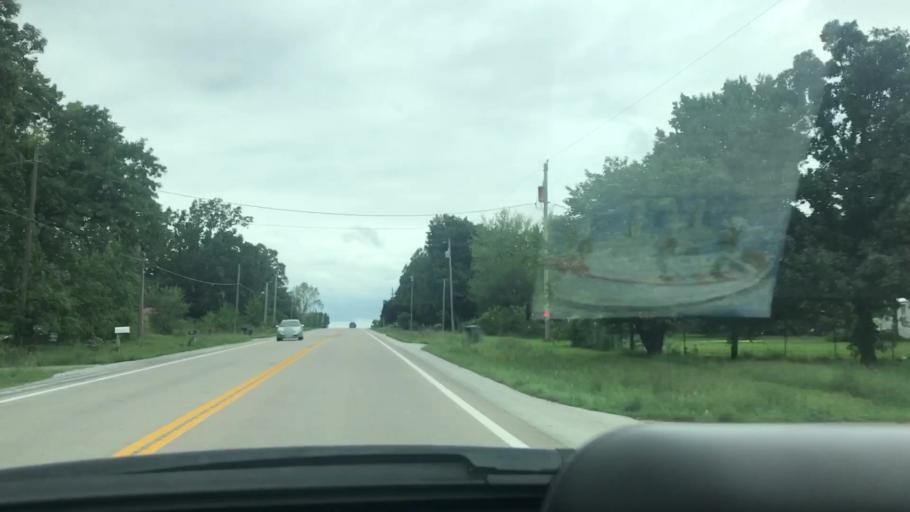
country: US
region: Missouri
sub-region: Dallas County
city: Buffalo
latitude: 37.7010
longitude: -93.1073
